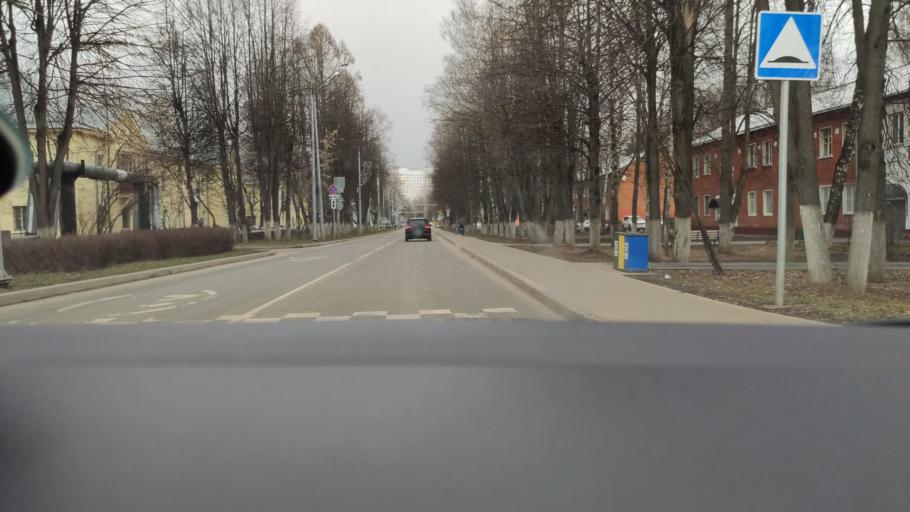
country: RU
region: Moskovskaya
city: Vatutinki
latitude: 55.5032
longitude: 37.3317
